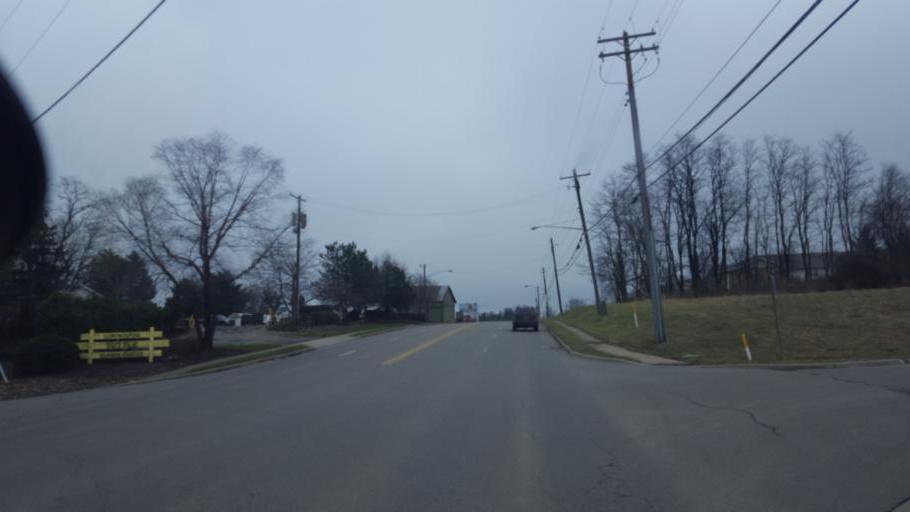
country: US
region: Ohio
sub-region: Richland County
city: Mansfield
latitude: 40.7244
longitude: -82.5460
